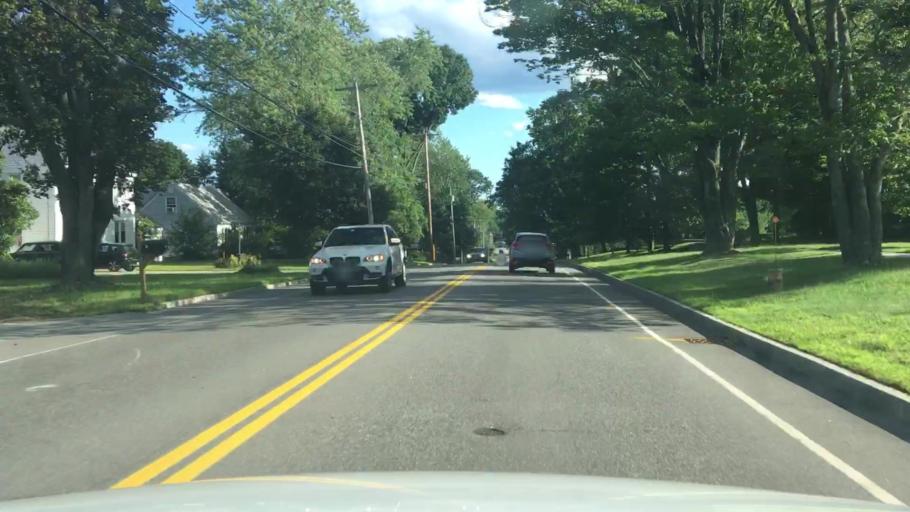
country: US
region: Maine
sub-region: Cumberland County
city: Scarborough
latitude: 43.5871
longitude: -70.3338
